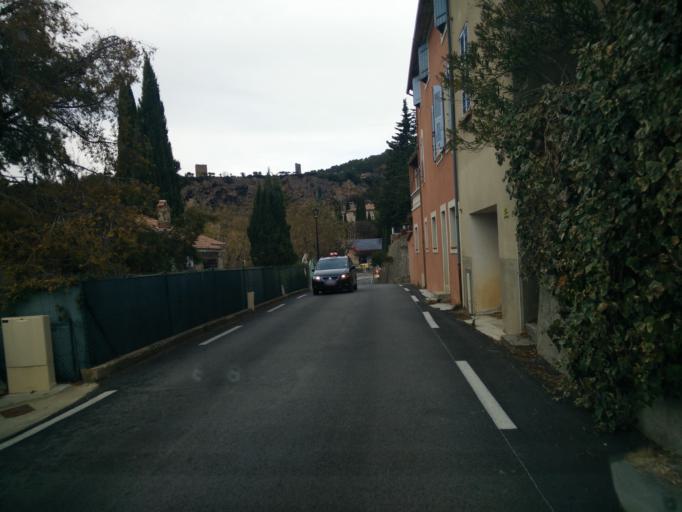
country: FR
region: Provence-Alpes-Cote d'Azur
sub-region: Departement du Var
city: Cotignac
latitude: 43.5261
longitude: 6.1526
